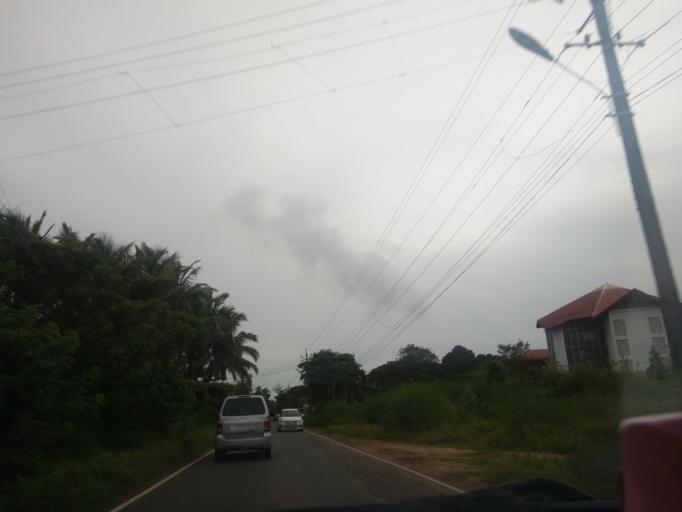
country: IN
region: Goa
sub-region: South Goa
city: Madgaon
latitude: 15.2589
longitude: 73.9698
